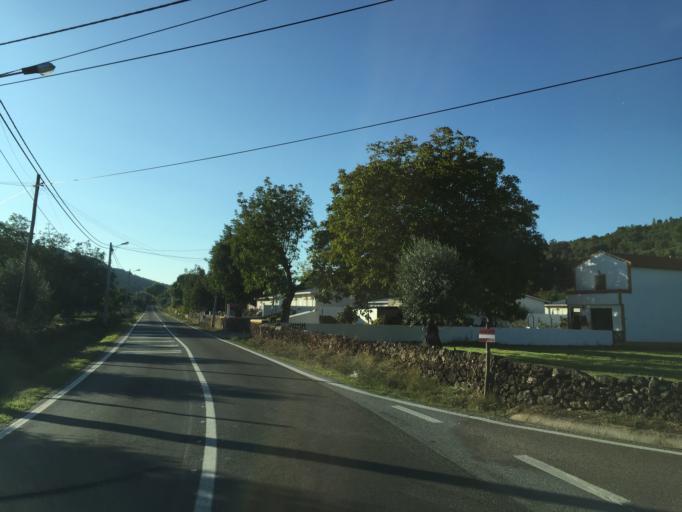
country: PT
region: Portalegre
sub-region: Marvao
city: Marvao
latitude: 39.3860
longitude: -7.3992
